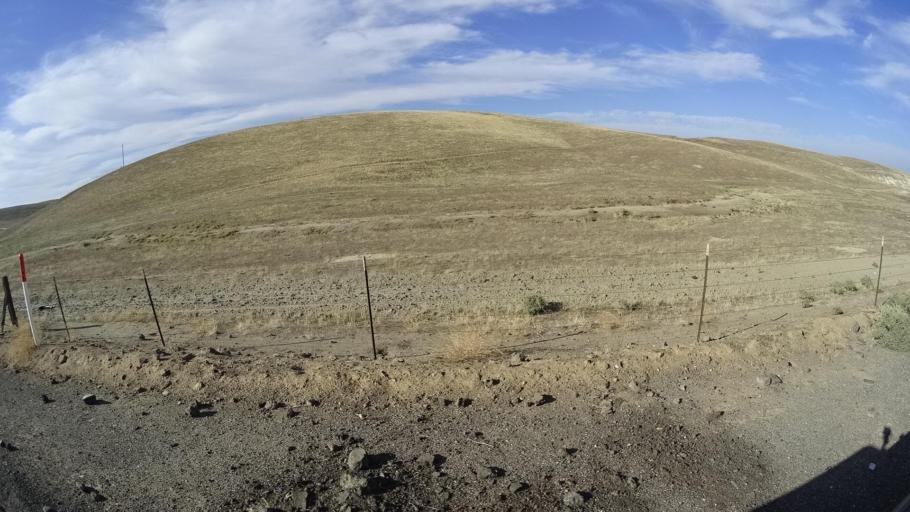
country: US
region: California
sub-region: Kern County
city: Oildale
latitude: 35.6187
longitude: -118.9868
